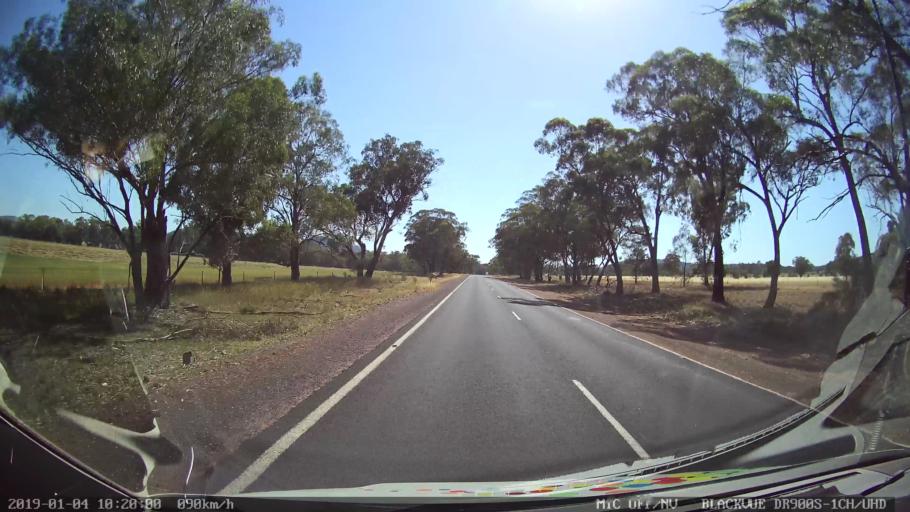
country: AU
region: New South Wales
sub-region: Cabonne
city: Canowindra
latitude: -33.3740
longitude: 148.4891
